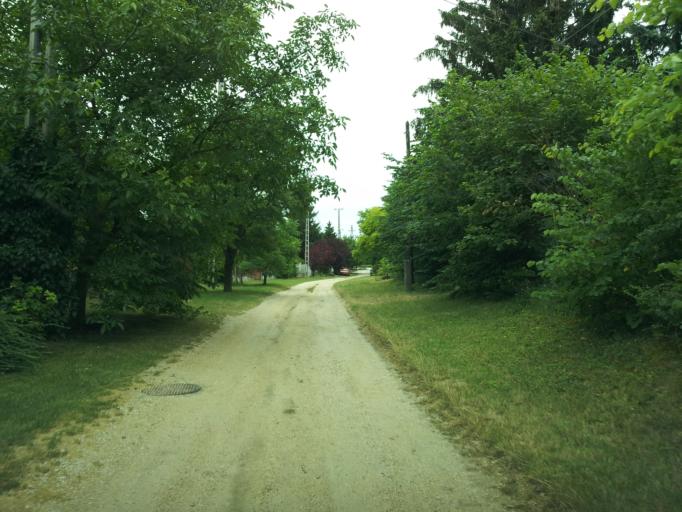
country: HU
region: Veszprem
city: Balatonkenese
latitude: 47.0189
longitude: 18.1655
